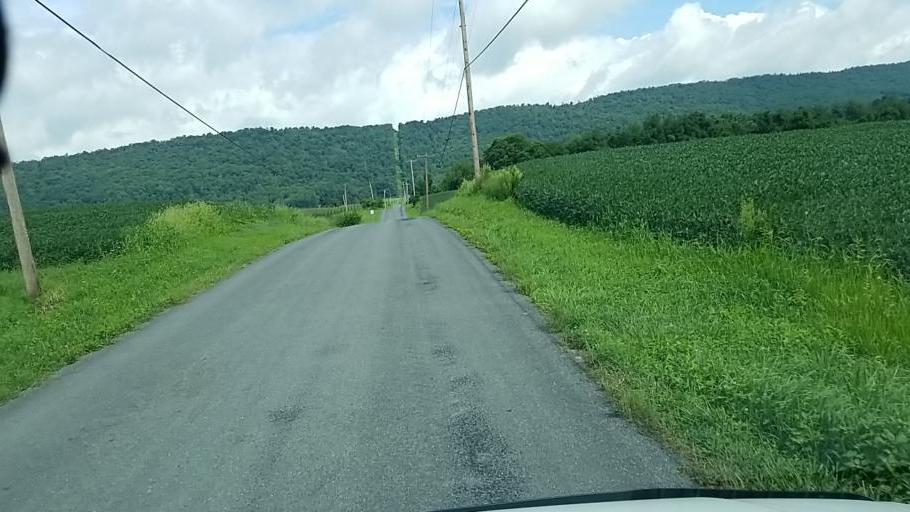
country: US
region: Pennsylvania
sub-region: Dauphin County
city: Millersburg
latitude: 40.5713
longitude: -76.9303
